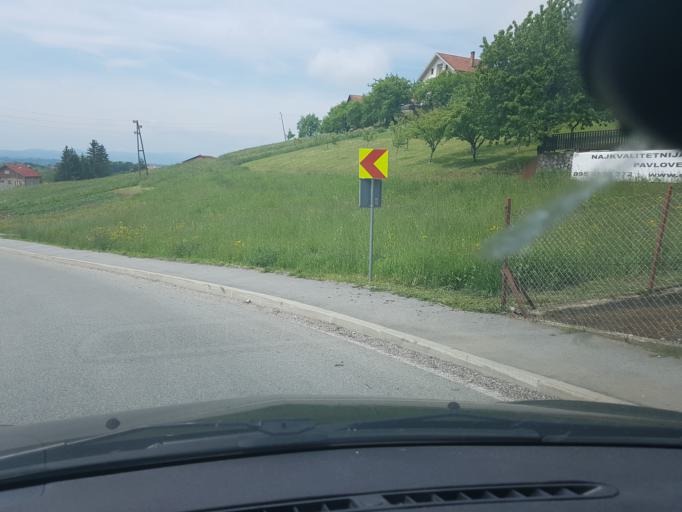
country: HR
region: Krapinsko-Zagorska
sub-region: Grad Krapina
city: Krapina
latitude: 46.1709
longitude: 15.8404
